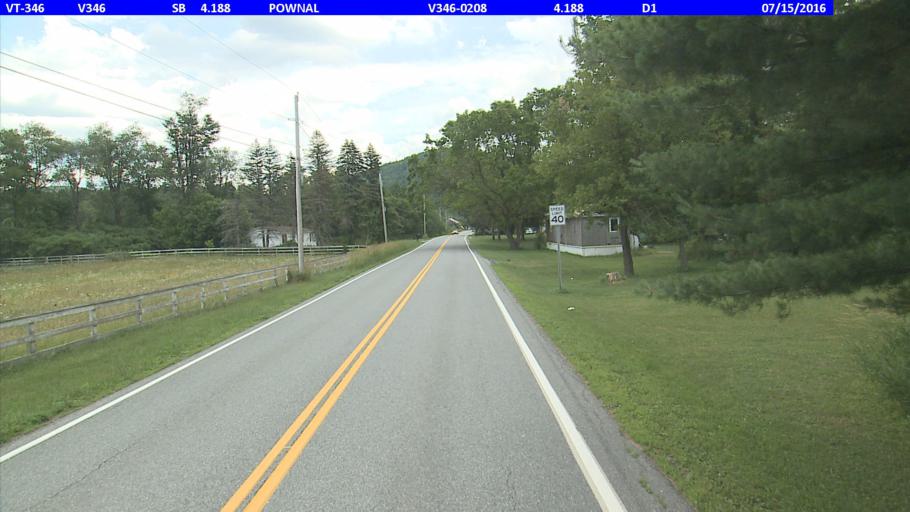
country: US
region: Vermont
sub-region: Bennington County
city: Bennington
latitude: 42.8083
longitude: -73.2780
